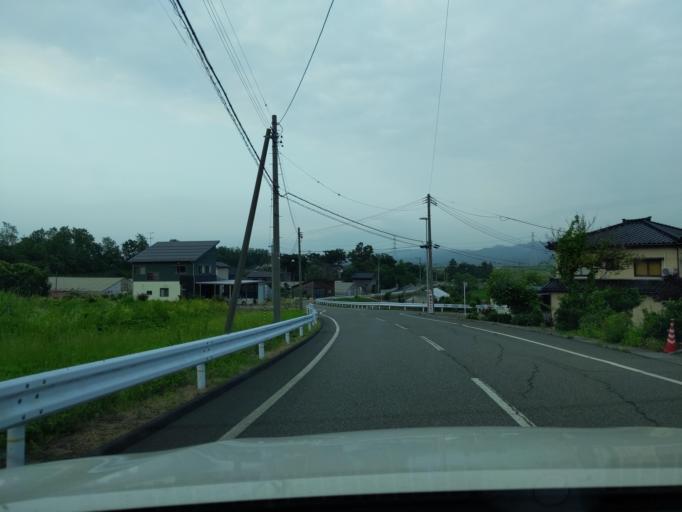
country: JP
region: Niigata
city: Kashiwazaki
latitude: 37.3981
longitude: 138.5964
